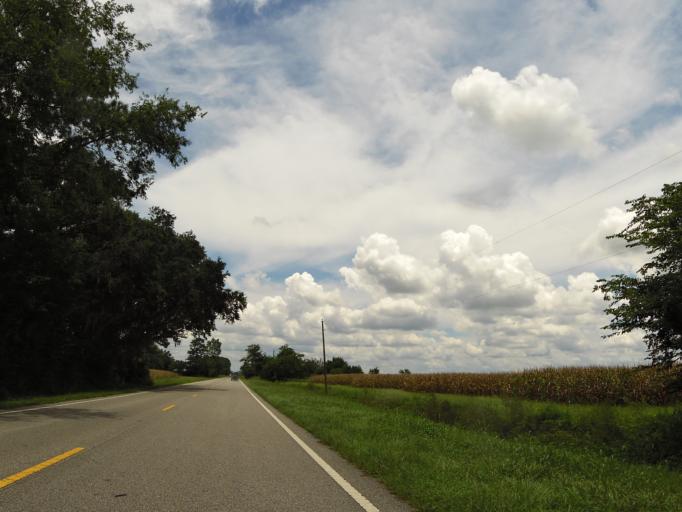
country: US
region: Florida
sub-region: Putnam County
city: East Palatka
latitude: 29.7021
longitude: -81.5008
